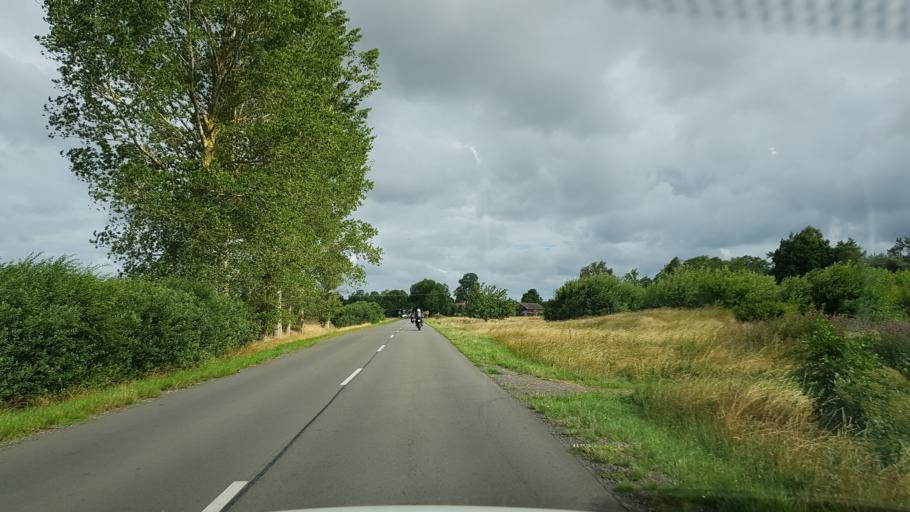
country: PL
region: West Pomeranian Voivodeship
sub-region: Powiat gryficki
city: Rewal
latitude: 54.0529
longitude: 15.0285
